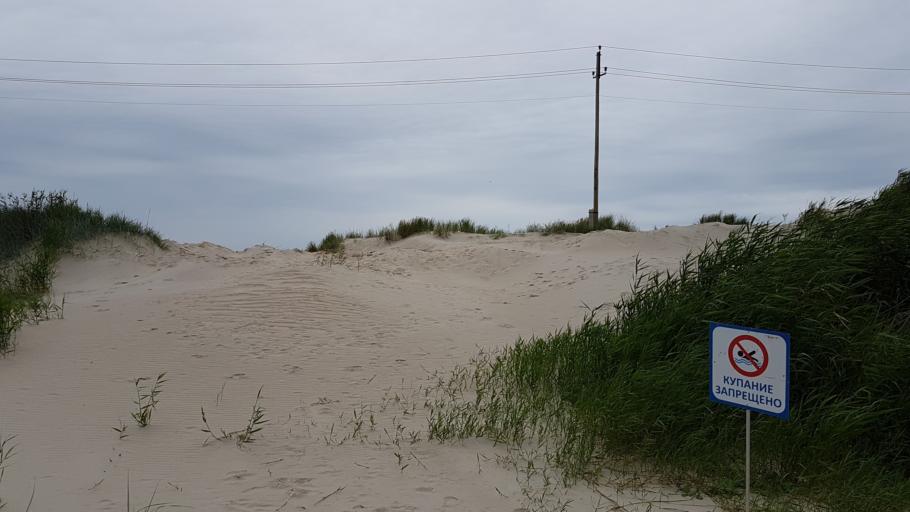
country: RU
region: Kaliningrad
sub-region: Gorod Kaliningrad
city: Yantarnyy
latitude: 54.8761
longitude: 19.9332
